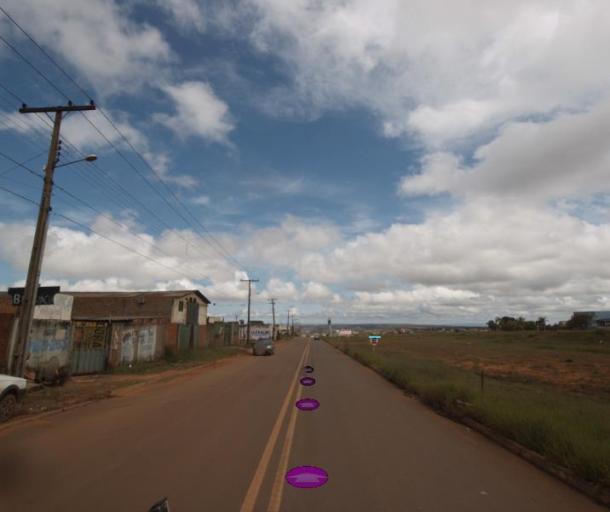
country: BR
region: Federal District
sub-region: Brasilia
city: Brasilia
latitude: -15.7384
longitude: -48.2943
